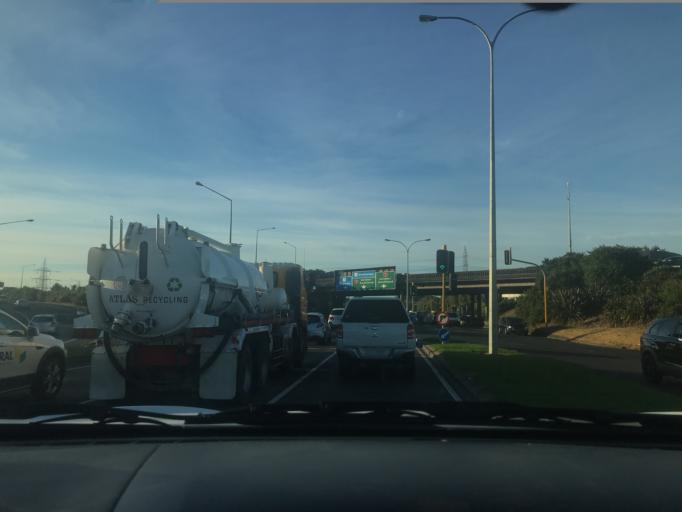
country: NZ
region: Auckland
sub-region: Auckland
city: Tamaki
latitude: -36.9180
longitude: 174.8398
